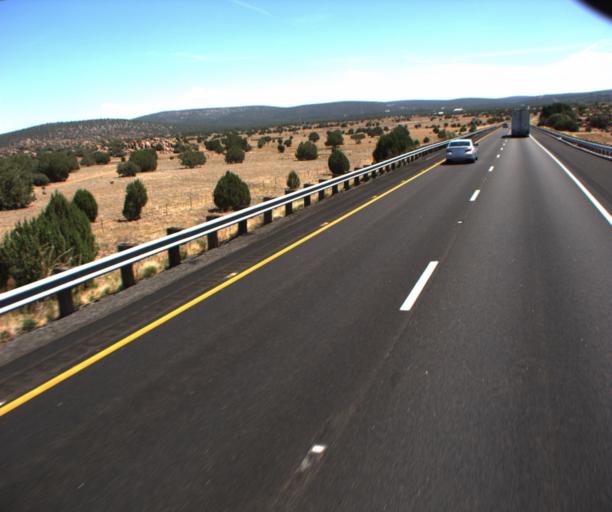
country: US
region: Arizona
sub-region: Mohave County
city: Peach Springs
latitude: 35.1859
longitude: -113.3808
